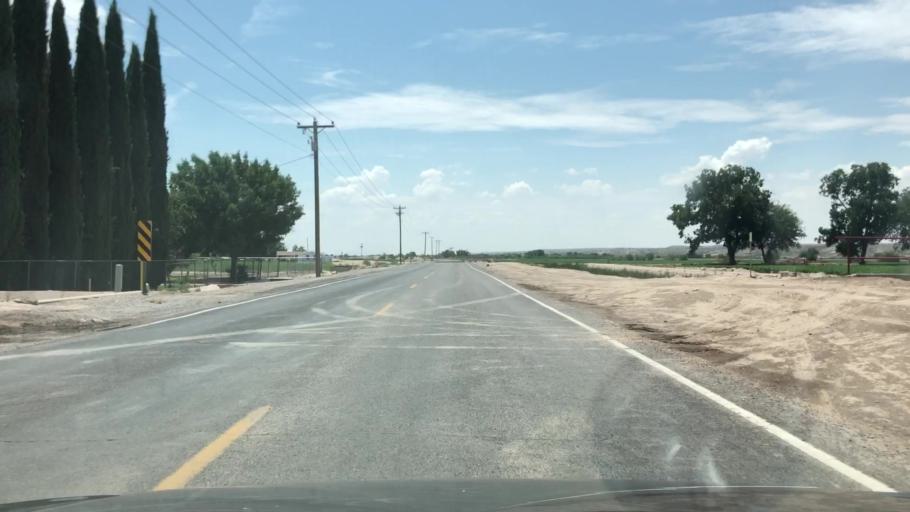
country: US
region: New Mexico
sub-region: Dona Ana County
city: Vado
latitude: 32.0765
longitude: -106.6836
